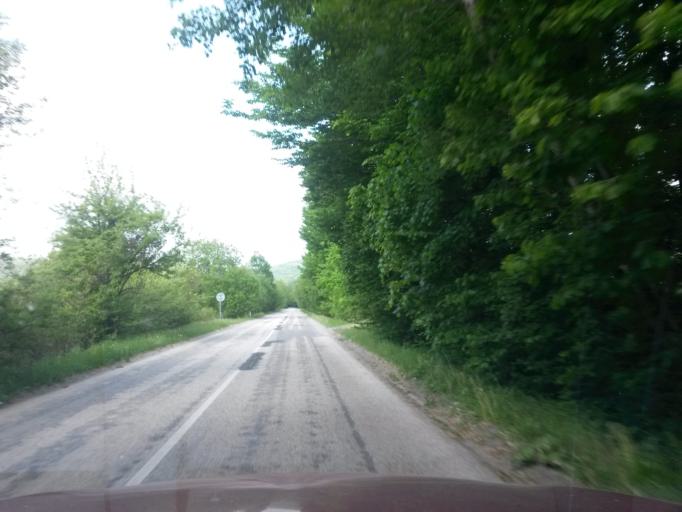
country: SK
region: Kosicky
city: Moldava nad Bodvou
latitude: 48.7310
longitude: 21.0949
